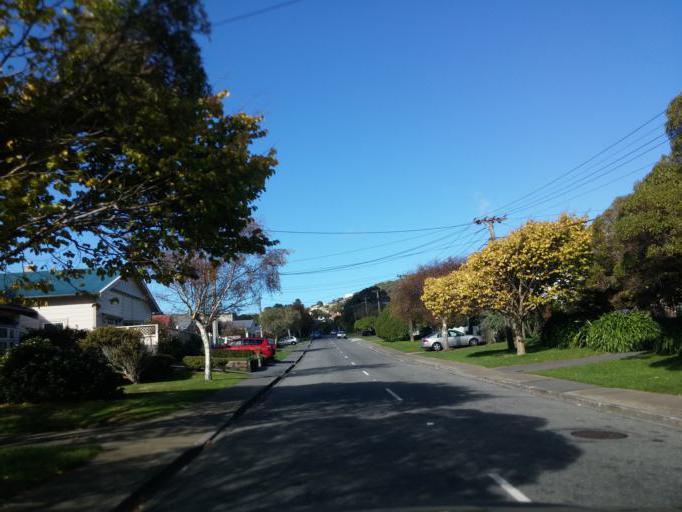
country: NZ
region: Wellington
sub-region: Wellington City
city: Kelburn
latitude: -41.2481
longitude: 174.7764
